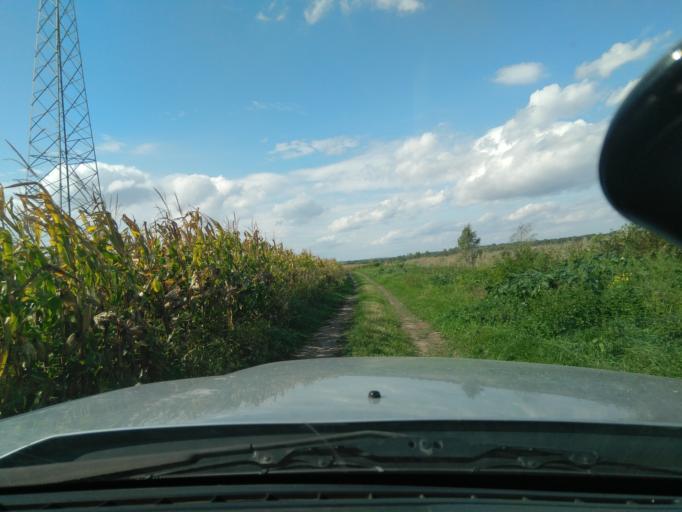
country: HU
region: Fejer
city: Bicske
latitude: 47.4783
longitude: 18.6685
